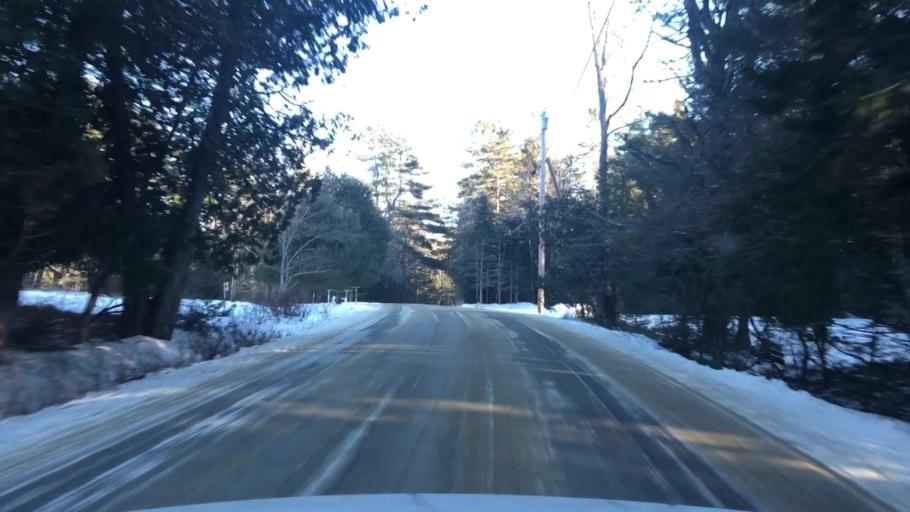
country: US
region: Maine
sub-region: Hancock County
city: Castine
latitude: 44.3842
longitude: -68.7358
